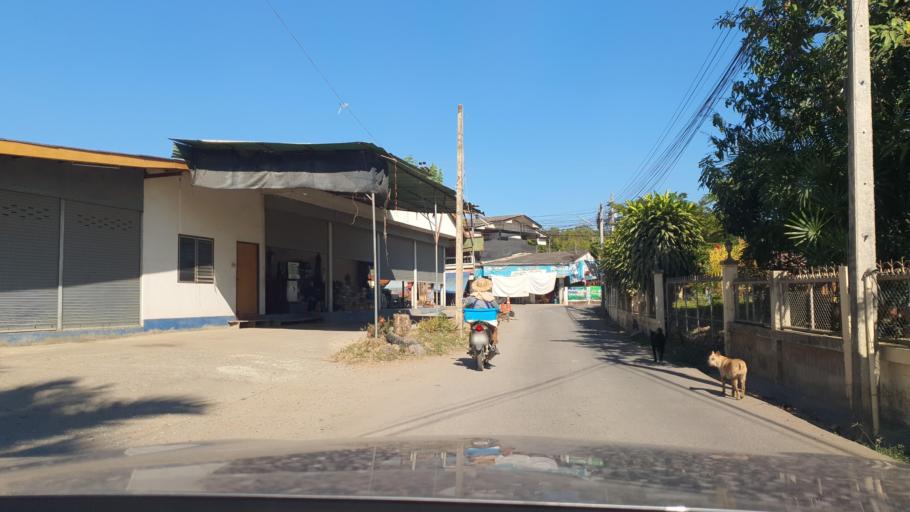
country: TH
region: Chiang Mai
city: San Pa Tong
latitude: 18.6667
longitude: 98.8339
